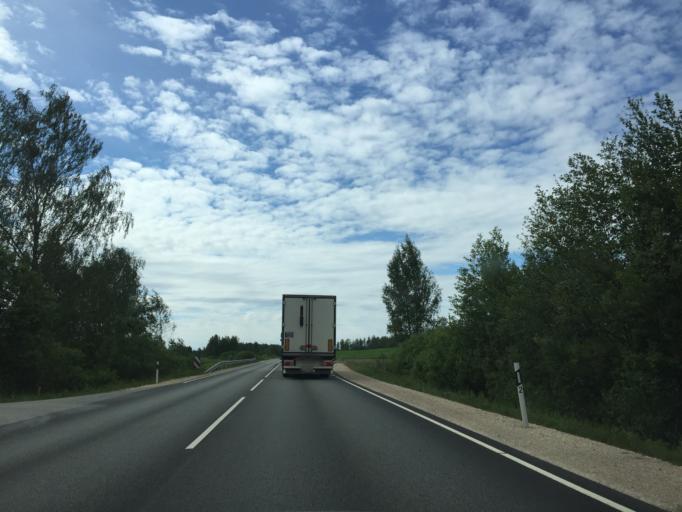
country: LV
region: Ikskile
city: Ikskile
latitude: 56.8812
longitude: 24.5095
